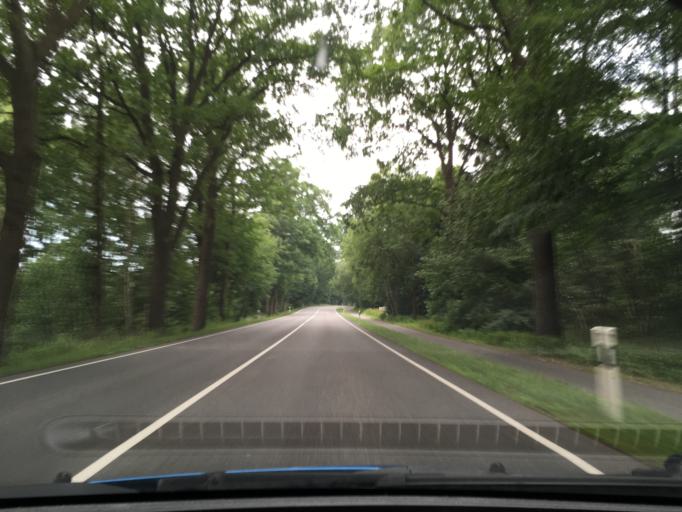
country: DE
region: Lower Saxony
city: Appel
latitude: 53.3983
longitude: 9.7900
